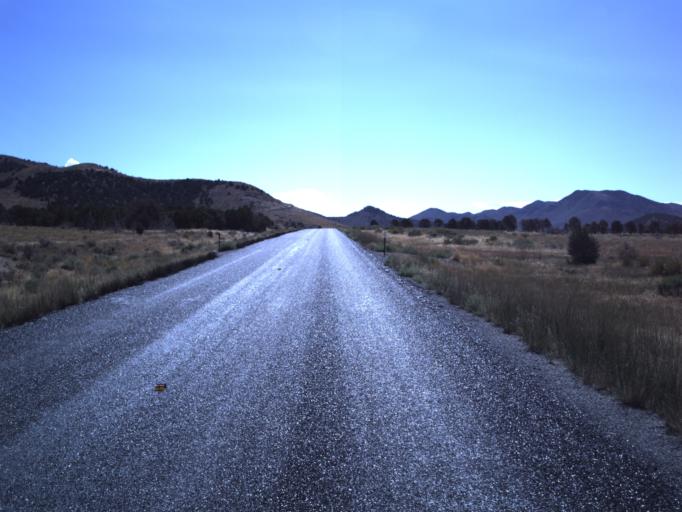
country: US
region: Utah
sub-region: Juab County
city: Mona
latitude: 39.9226
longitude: -112.1515
